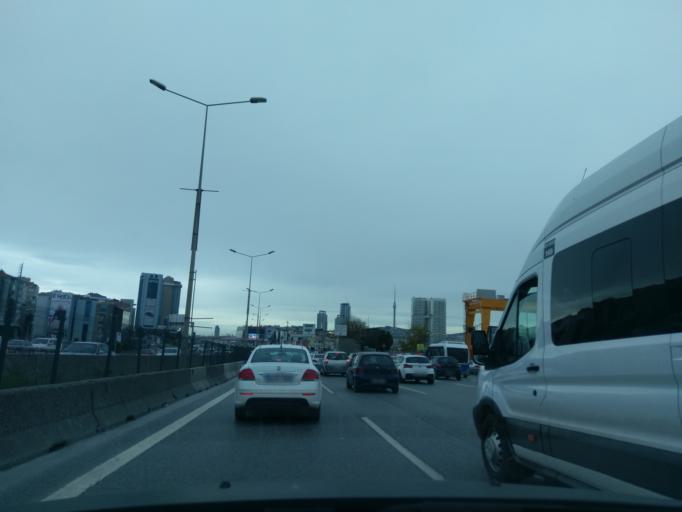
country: TR
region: Istanbul
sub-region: Atasehir
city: Atasehir
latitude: 40.9838
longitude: 29.0924
